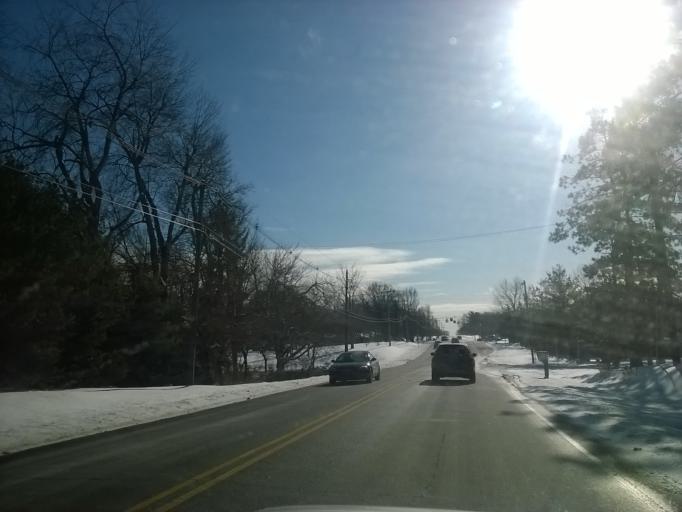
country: US
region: Indiana
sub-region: Hamilton County
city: Carmel
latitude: 39.9433
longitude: -86.1269
